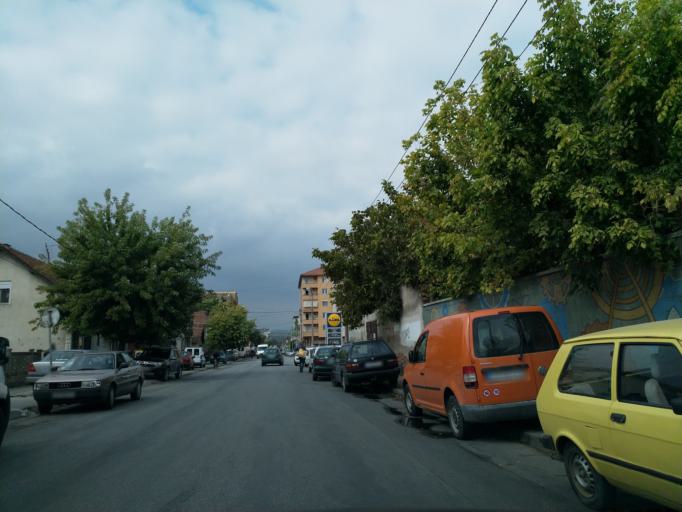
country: RS
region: Central Serbia
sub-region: Pomoravski Okrug
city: Jagodina
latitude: 43.9837
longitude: 21.2573
